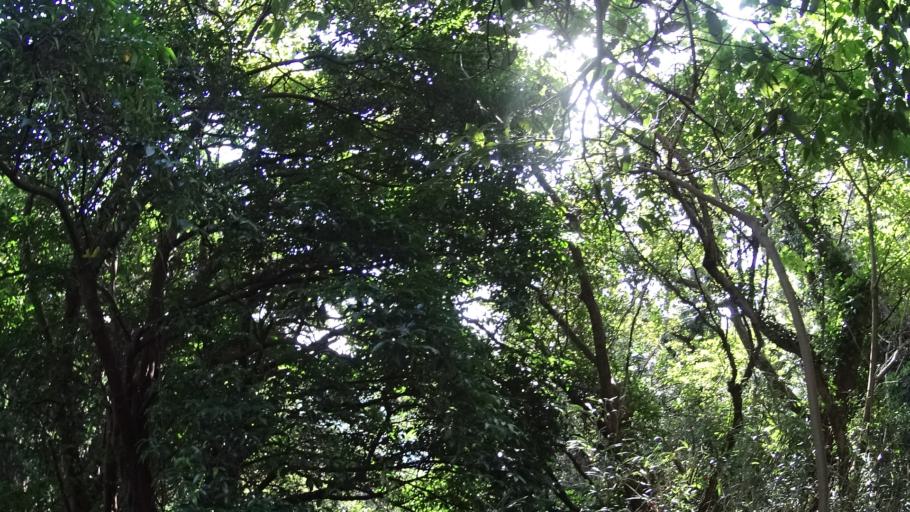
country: JP
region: Kanagawa
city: Hayama
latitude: 35.2780
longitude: 139.6124
